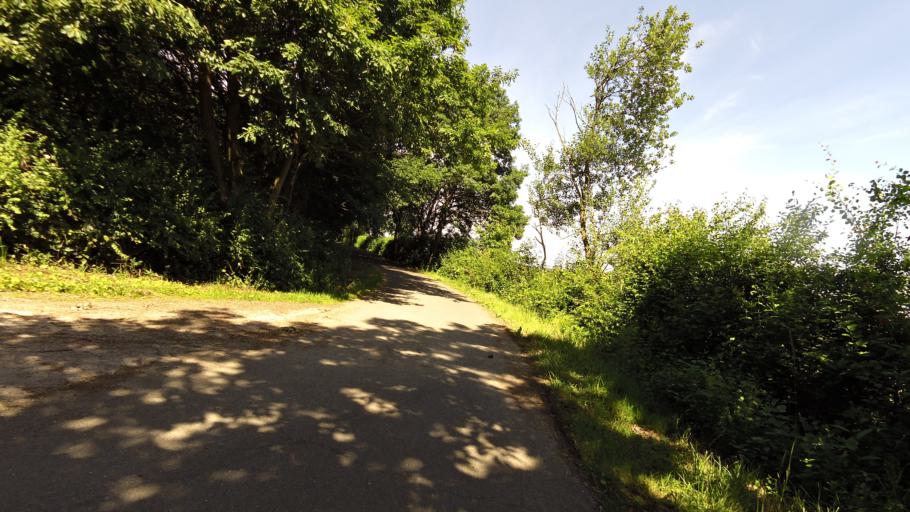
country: DE
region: North Rhine-Westphalia
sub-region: Regierungsbezirk Koln
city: Rheinbach
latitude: 50.6074
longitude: 6.9736
